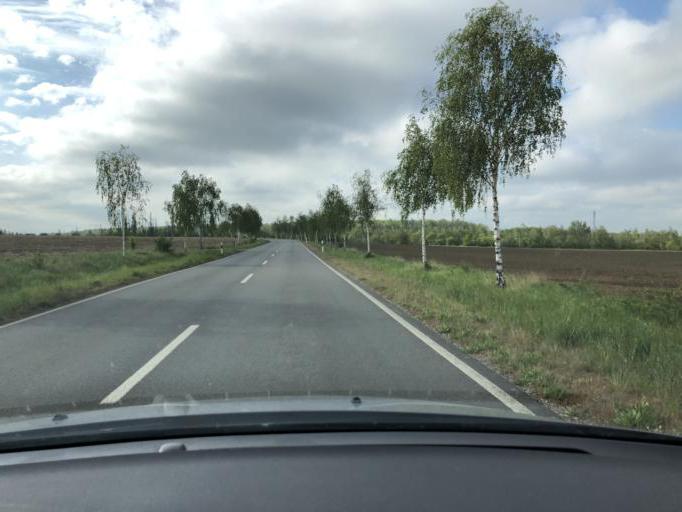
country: DE
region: Saxony
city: Neukieritzsch
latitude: 51.1569
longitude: 12.4218
